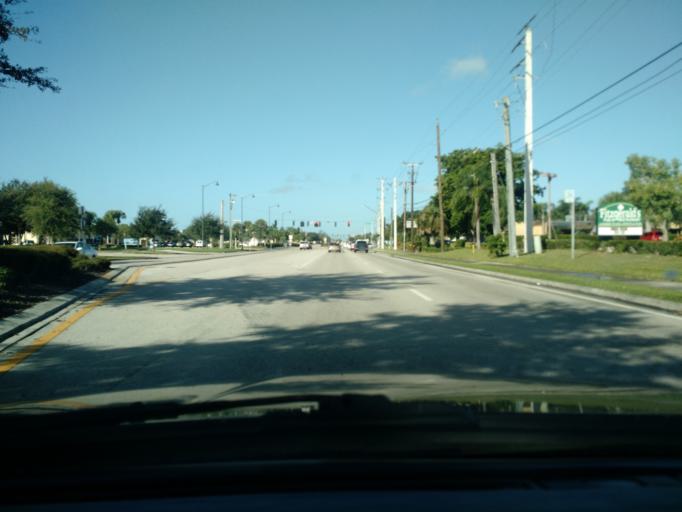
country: US
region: Florida
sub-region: Lee County
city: Bonita Springs
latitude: 26.3307
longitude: -81.8014
